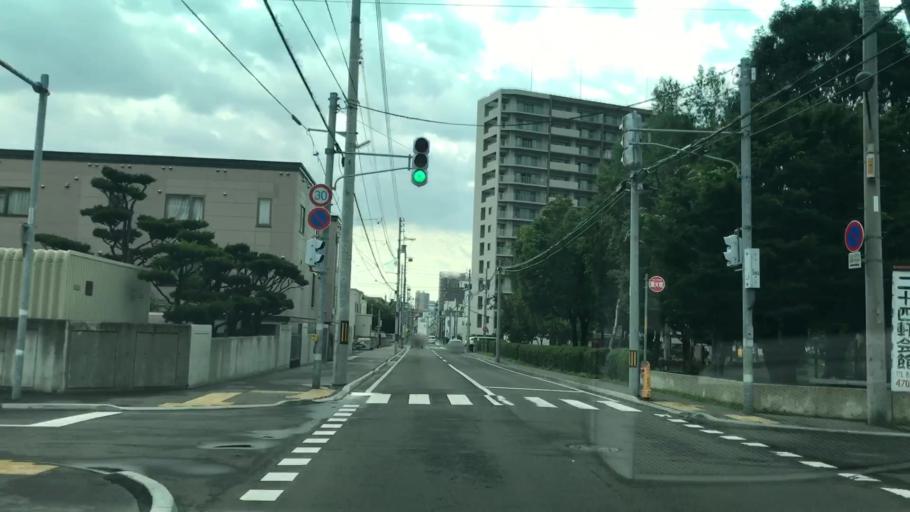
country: JP
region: Hokkaido
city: Sapporo
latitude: 43.0743
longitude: 141.3103
